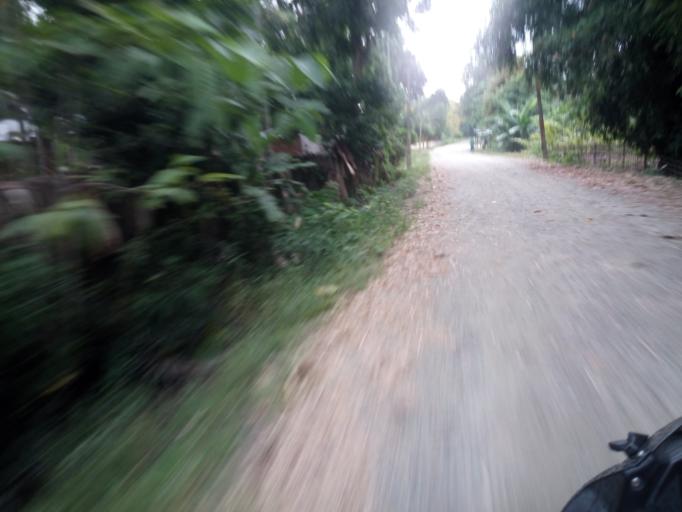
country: IN
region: Assam
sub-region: Darrang
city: Kharupatia
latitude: 26.6511
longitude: 92.2430
